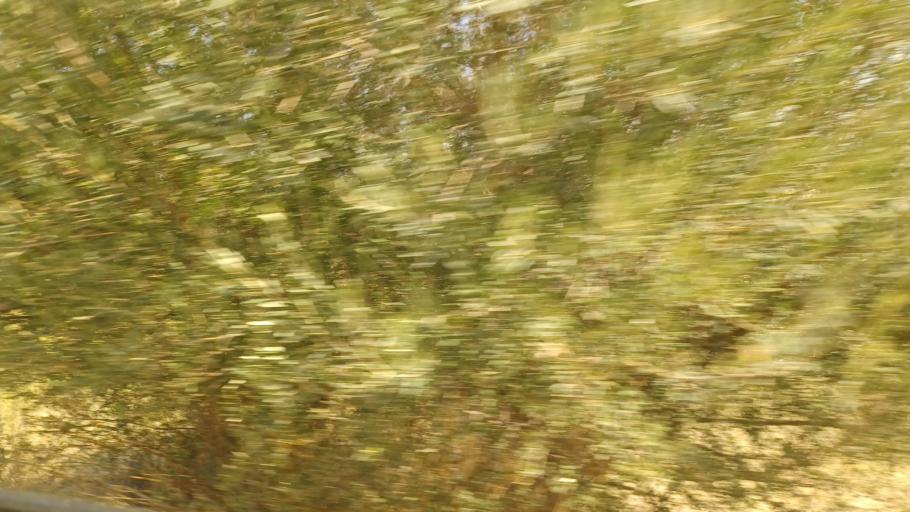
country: CY
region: Pafos
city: Polis
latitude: 34.9996
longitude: 32.4338
